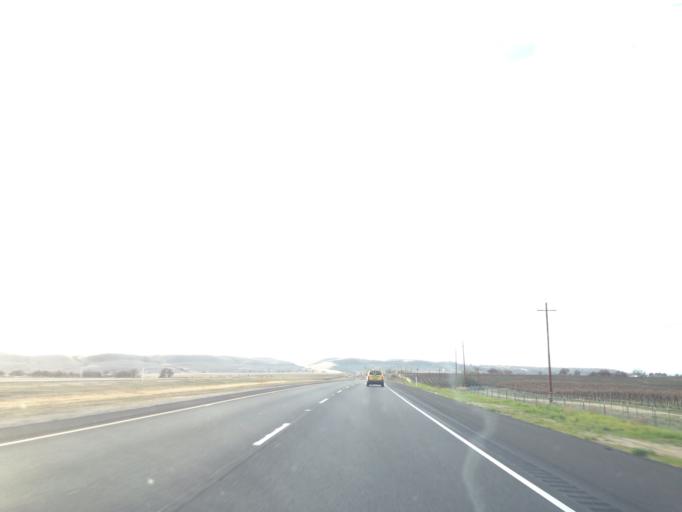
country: US
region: California
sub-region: San Luis Obispo County
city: Shandon
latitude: 35.6591
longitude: -120.4823
